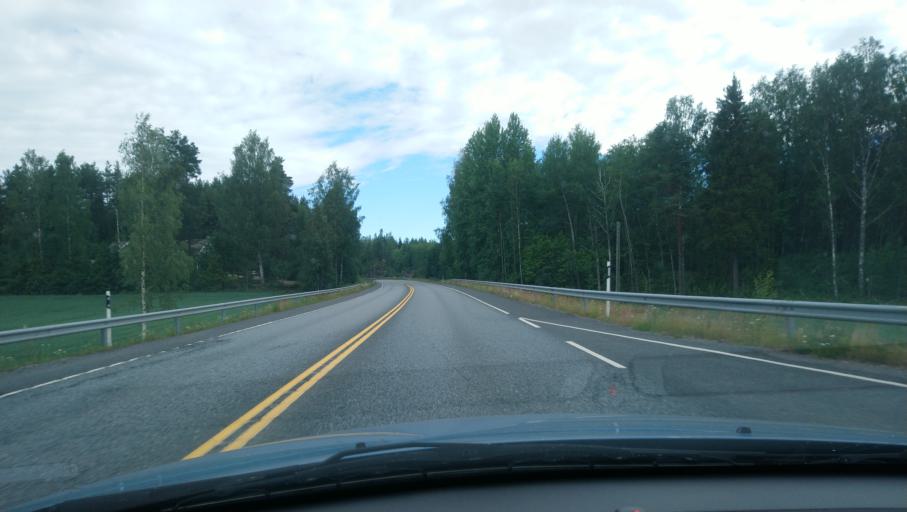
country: FI
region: Uusimaa
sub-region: Porvoo
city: Porvoo
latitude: 60.4227
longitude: 25.5795
